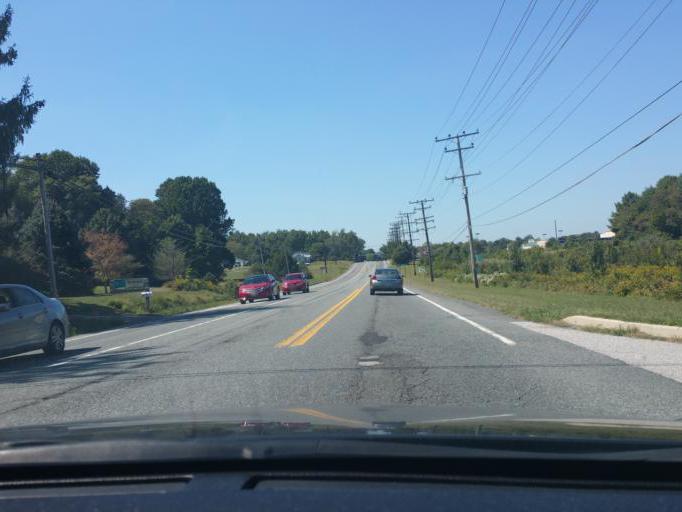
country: US
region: Maryland
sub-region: Harford County
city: Bel Air South
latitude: 39.5558
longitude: -76.2675
